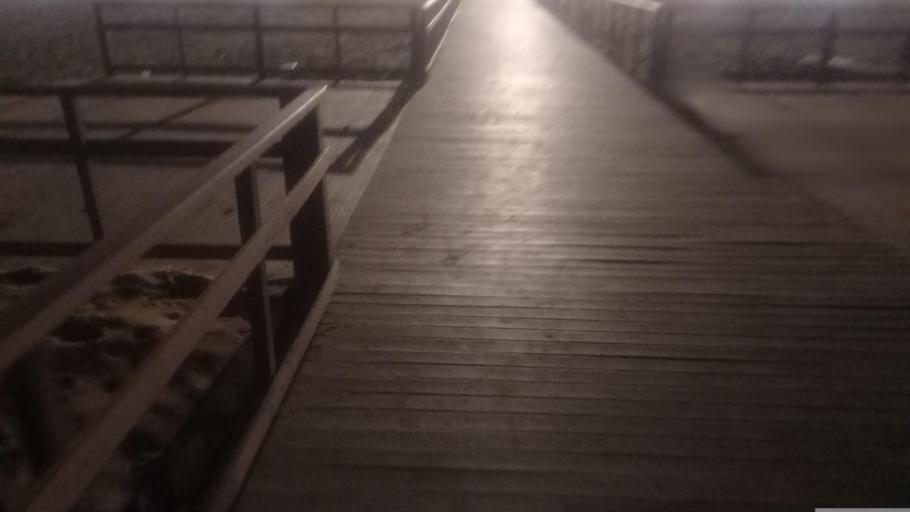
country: IN
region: Tamil Nadu
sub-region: Chennai
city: Chennai
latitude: 13.0488
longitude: 80.2825
